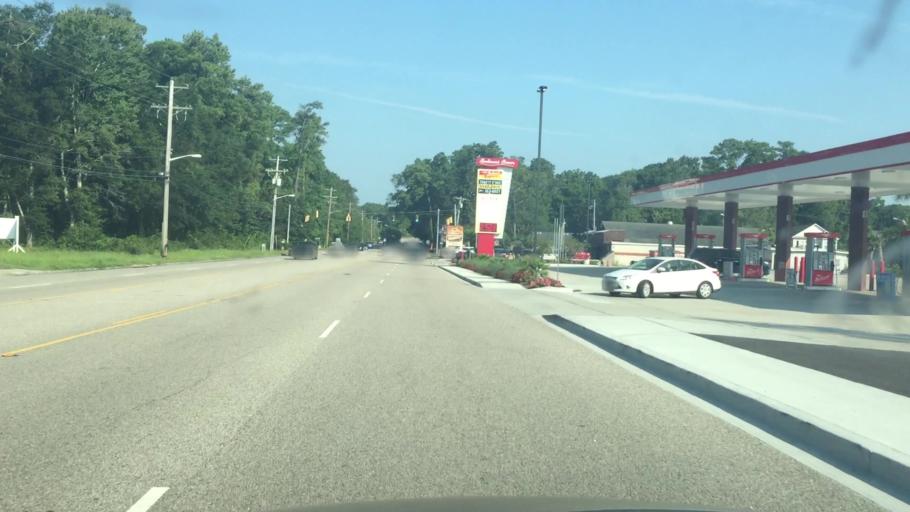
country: US
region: South Carolina
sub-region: Horry County
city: North Myrtle Beach
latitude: 33.8414
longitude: -78.6468
